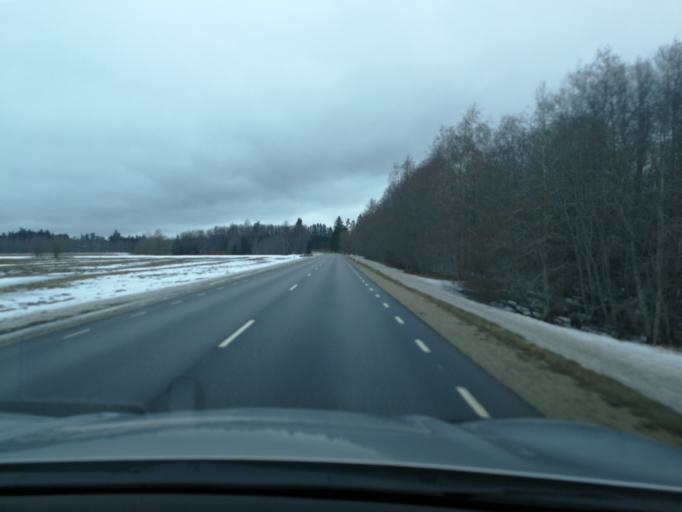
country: EE
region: Harju
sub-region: Anija vald
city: Kehra
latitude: 59.2884
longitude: 25.3752
